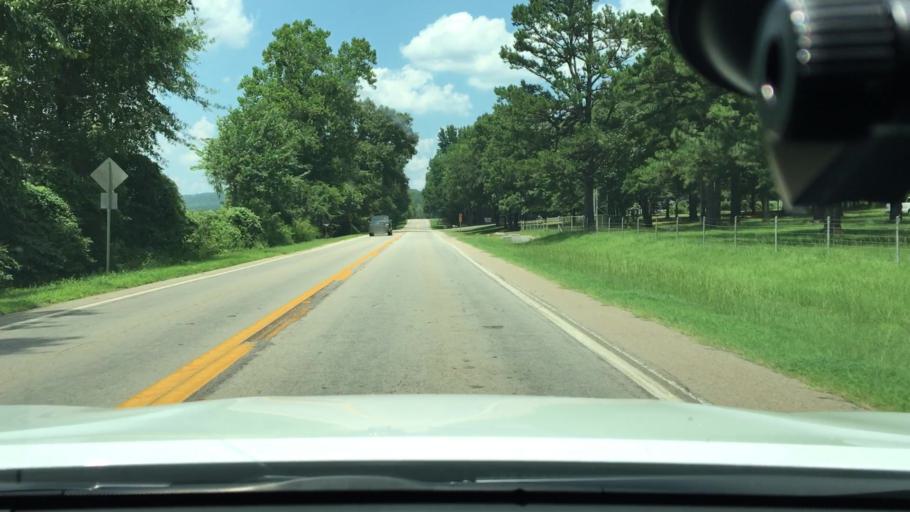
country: US
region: Arkansas
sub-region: Logan County
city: Booneville
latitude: 35.2108
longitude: -93.9285
